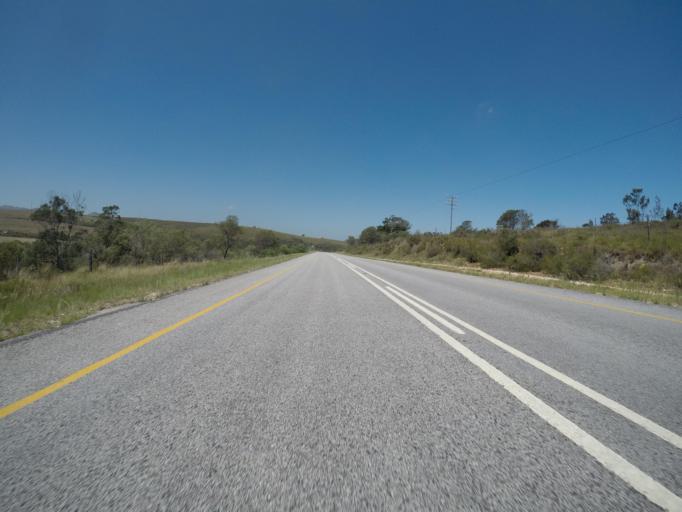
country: ZA
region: Eastern Cape
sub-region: Cacadu District Municipality
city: Kruisfontein
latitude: -34.0198
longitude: 24.5808
